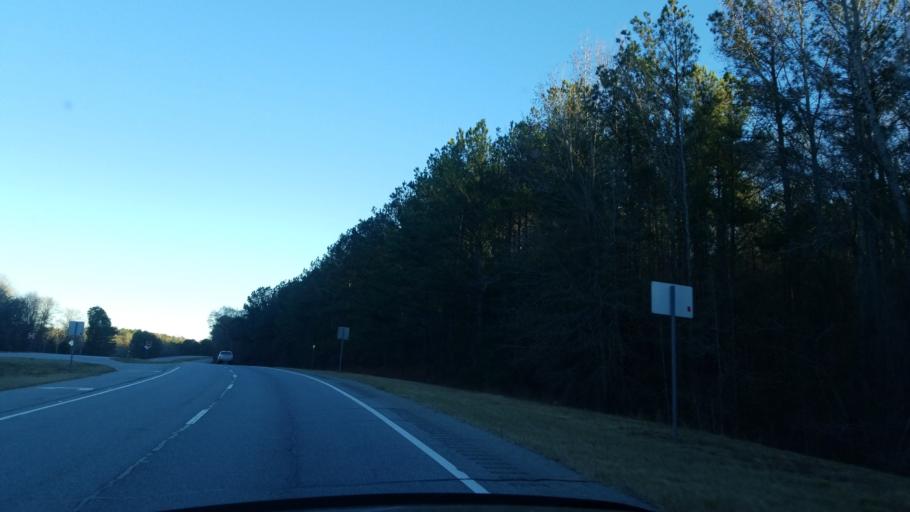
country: US
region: Georgia
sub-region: Chattahoochee County
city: Cusseta
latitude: 32.2642
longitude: -84.7395
